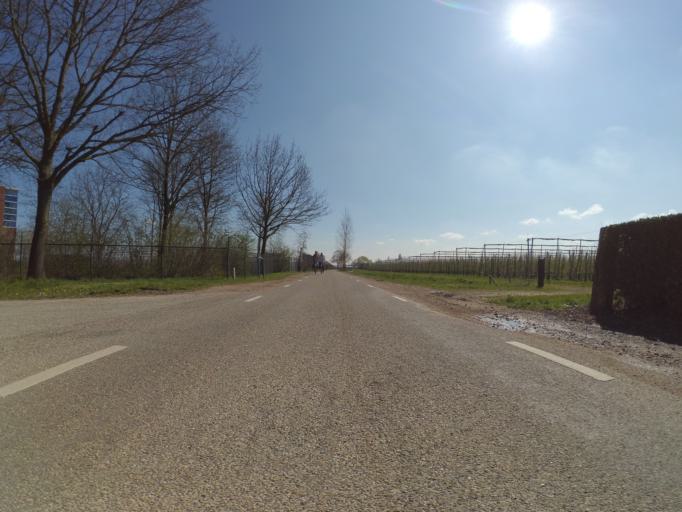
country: NL
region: Utrecht
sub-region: Gemeente Wijk bij Duurstede
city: Wijk bij Duurstede
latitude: 51.9869
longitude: 5.3059
